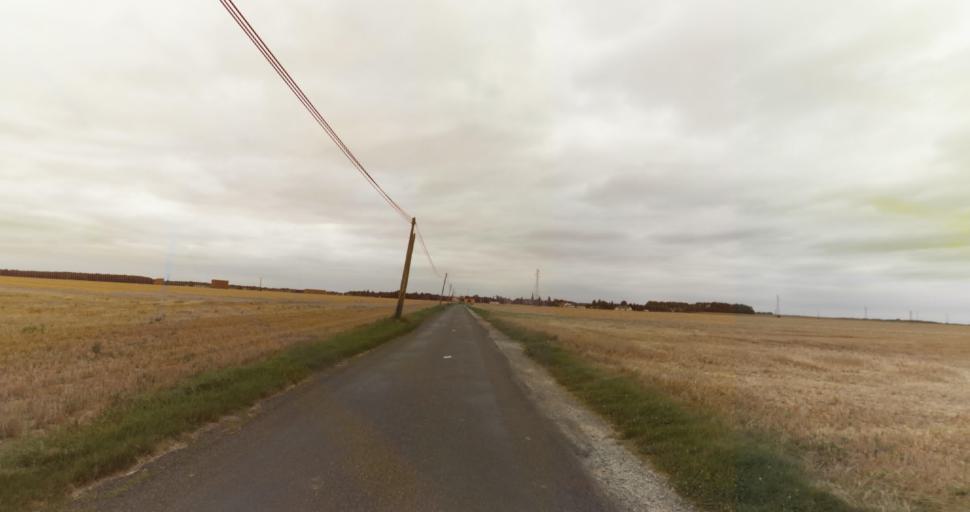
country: FR
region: Haute-Normandie
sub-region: Departement de l'Eure
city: Menilles
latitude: 48.9480
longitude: 1.2654
